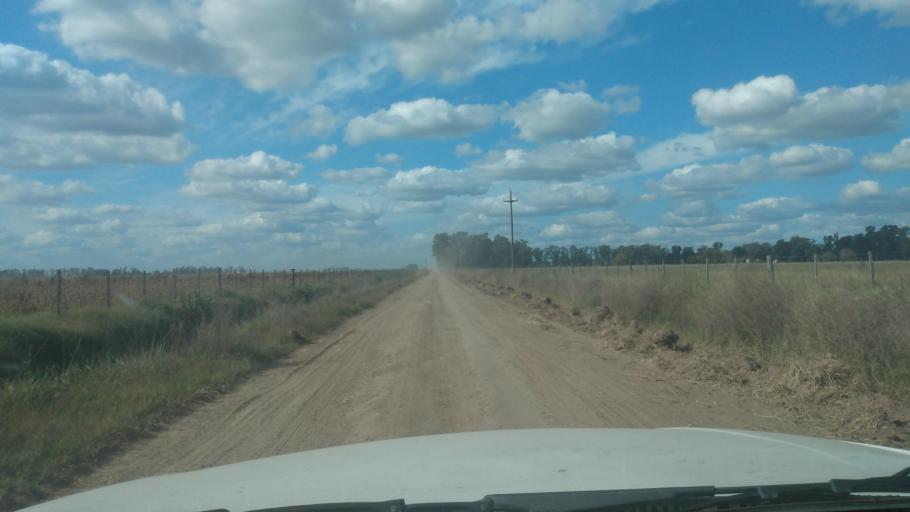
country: AR
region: Buenos Aires
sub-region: Partido de Navarro
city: Navarro
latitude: -35.0338
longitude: -59.5027
